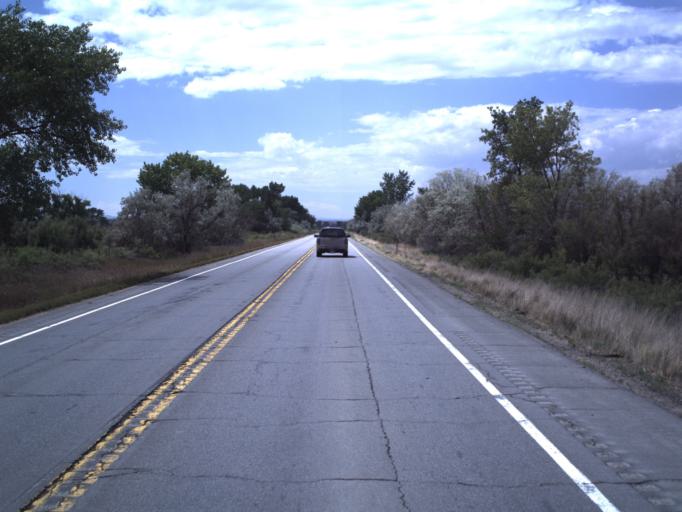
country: US
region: Utah
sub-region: Duchesne County
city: Duchesne
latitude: 40.1578
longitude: -110.1778
